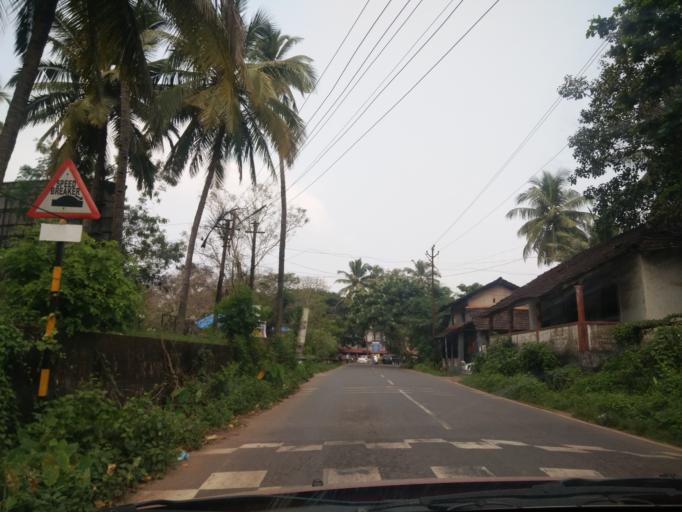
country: IN
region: Goa
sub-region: North Goa
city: Goa Velha
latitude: 15.4261
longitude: 73.8990
